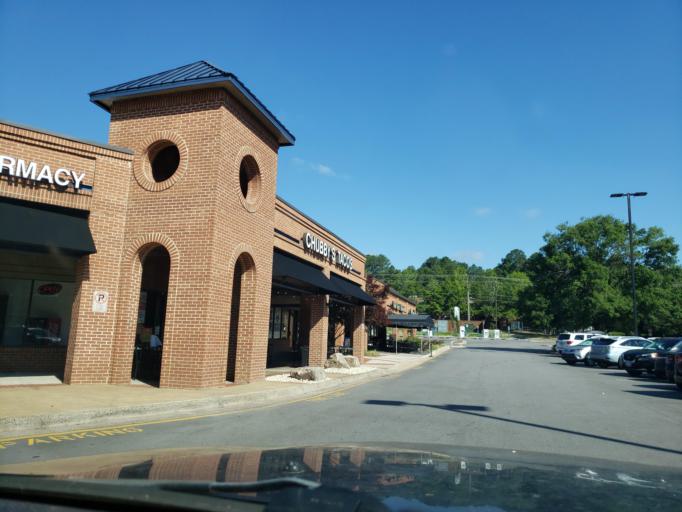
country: US
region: North Carolina
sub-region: Durham County
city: Durham
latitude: 35.9207
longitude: -78.9570
